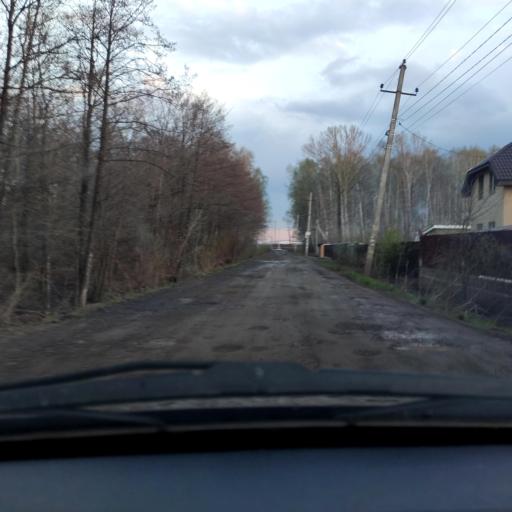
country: RU
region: Bashkortostan
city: Ufa
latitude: 54.6299
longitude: 55.8901
